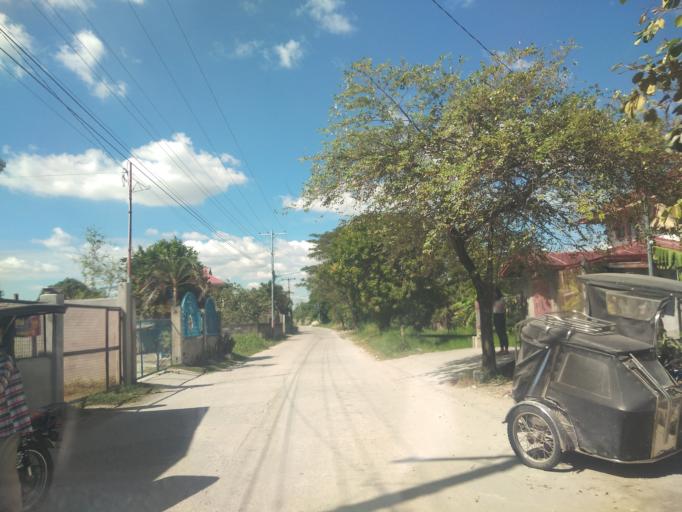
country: PH
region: Central Luzon
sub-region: Province of Pampanga
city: Bacolor
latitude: 15.0126
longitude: 120.6433
